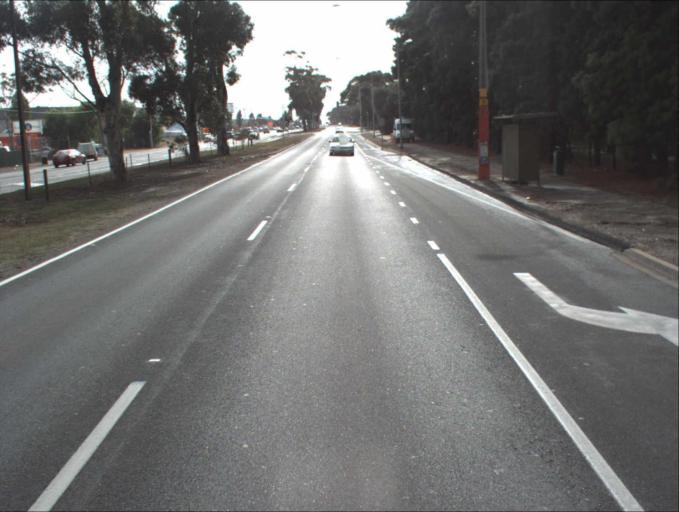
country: AU
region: South Australia
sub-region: Port Adelaide Enfield
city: Enfield
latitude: -34.8408
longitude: 138.6057
